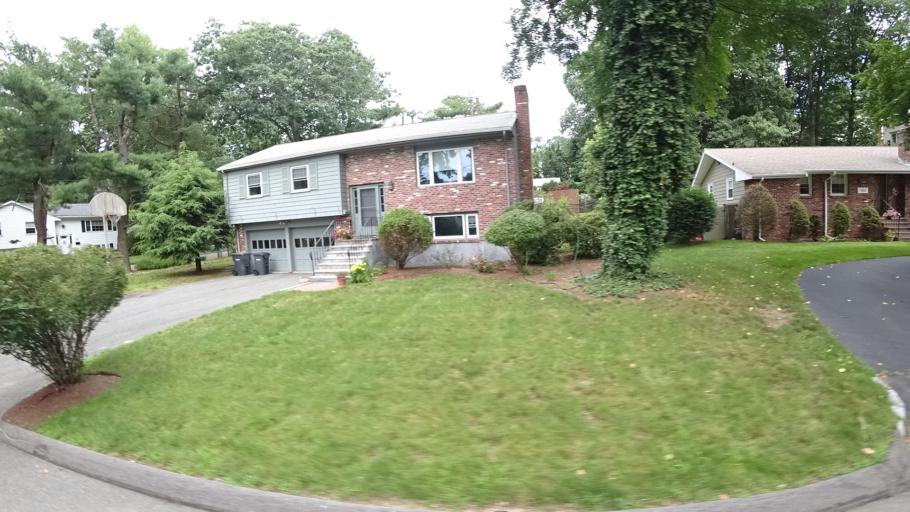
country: US
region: Massachusetts
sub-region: Norfolk County
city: Dedham
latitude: 42.2257
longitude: -71.1510
